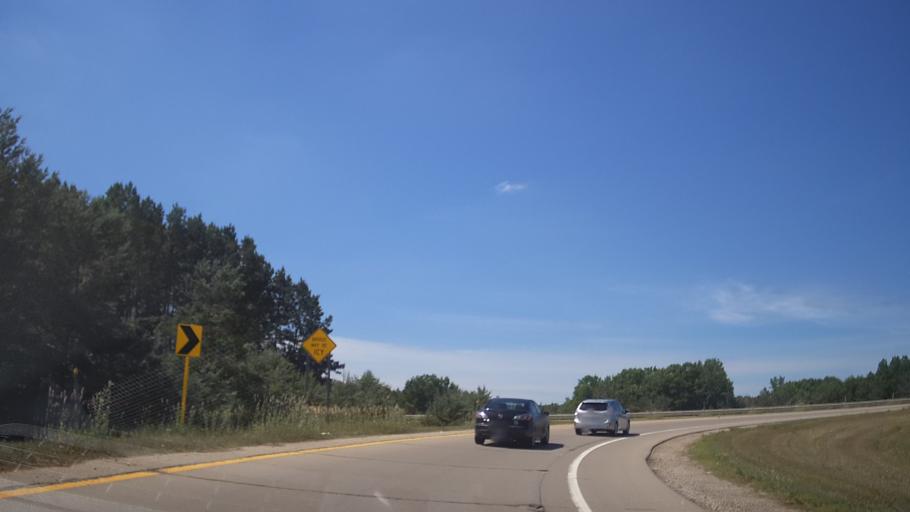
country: US
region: Michigan
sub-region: Clare County
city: Clare
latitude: 43.8631
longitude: -84.9109
